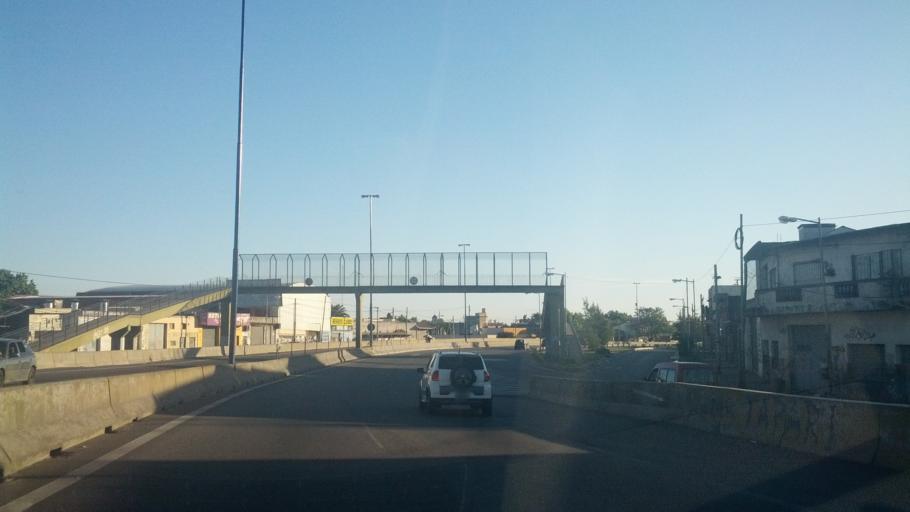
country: AR
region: Buenos Aires
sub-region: Partido de Lomas de Zamora
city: Lomas de Zamora
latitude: -34.7471
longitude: -58.4302
